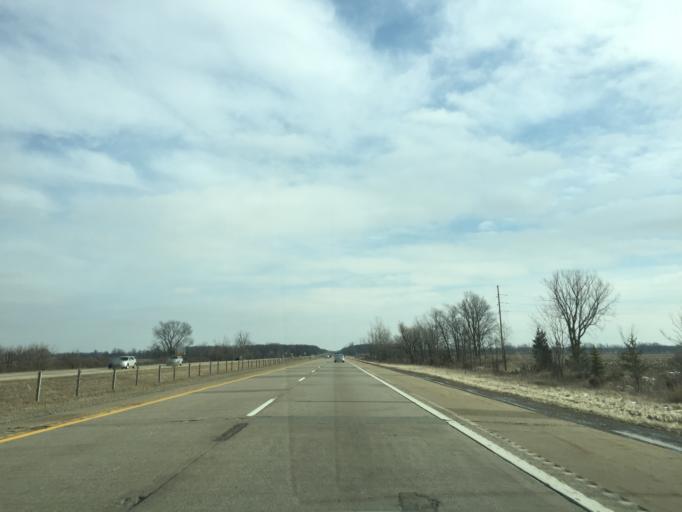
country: US
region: Michigan
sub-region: Ionia County
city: Ionia
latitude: 42.8789
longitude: -85.0268
